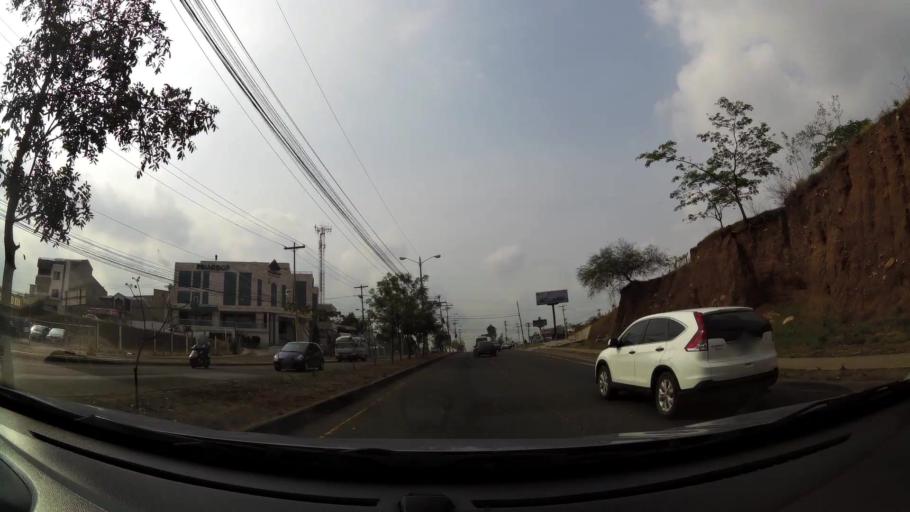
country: HN
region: Francisco Morazan
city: Santa Lucia
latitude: 14.1042
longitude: -87.1602
